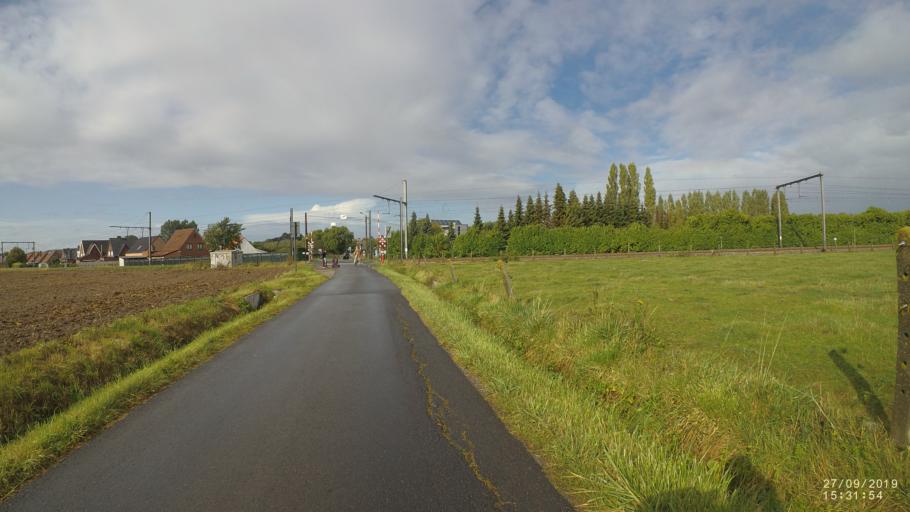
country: BE
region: Flanders
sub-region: Provincie Oost-Vlaanderen
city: Zottegem
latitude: 50.8744
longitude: 3.7404
